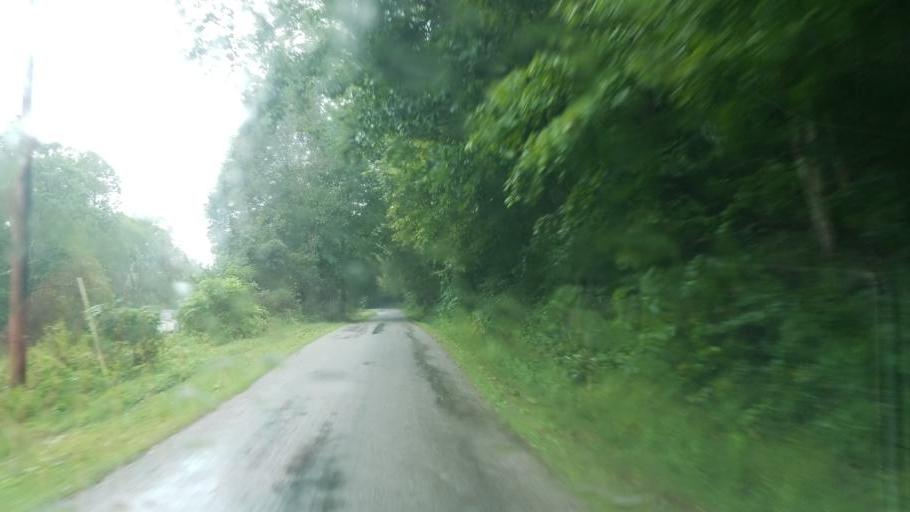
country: US
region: Kentucky
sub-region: Lewis County
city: Vanceburg
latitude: 38.7931
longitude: -83.2564
